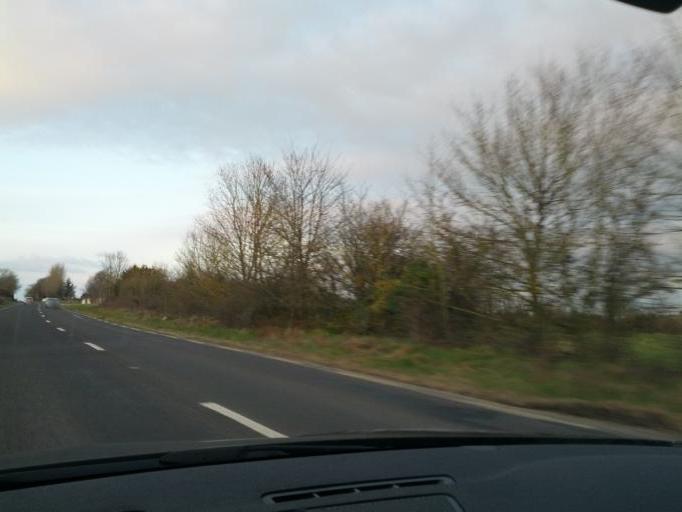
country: IE
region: Munster
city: Nenagh Bridge
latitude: 52.9048
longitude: -8.1839
